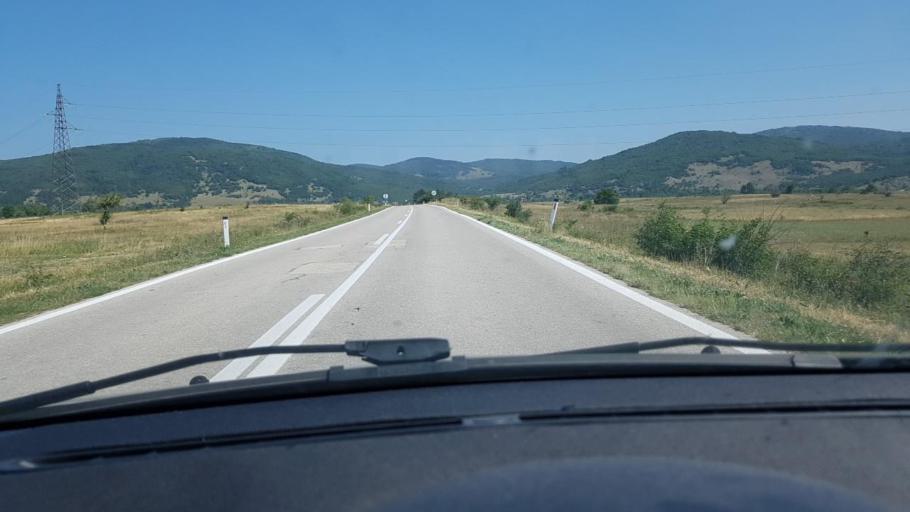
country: BA
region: Federation of Bosnia and Herzegovina
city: Bosansko Grahovo
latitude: 44.2757
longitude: 16.3010
